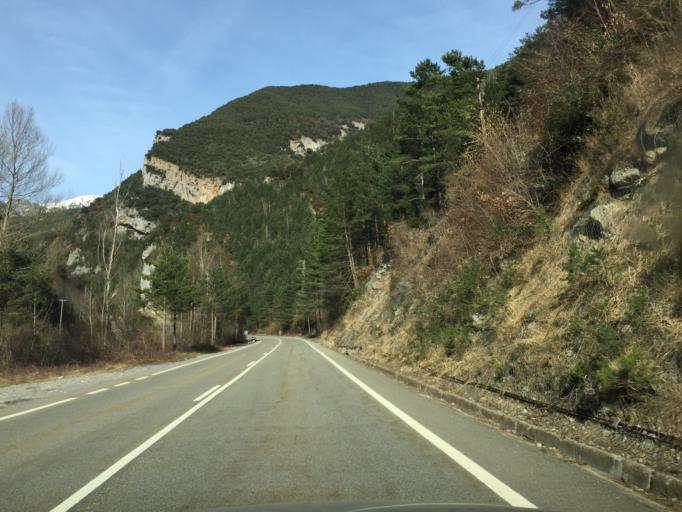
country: ES
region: Aragon
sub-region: Provincia de Huesca
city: Bielsa
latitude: 42.5989
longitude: 0.2391
